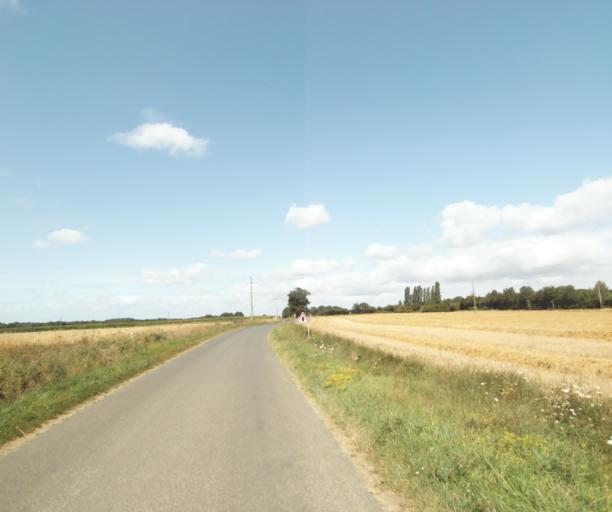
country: FR
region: Pays de la Loire
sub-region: Departement de la Sarthe
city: Sable-sur-Sarthe
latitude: 47.8502
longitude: -0.3944
